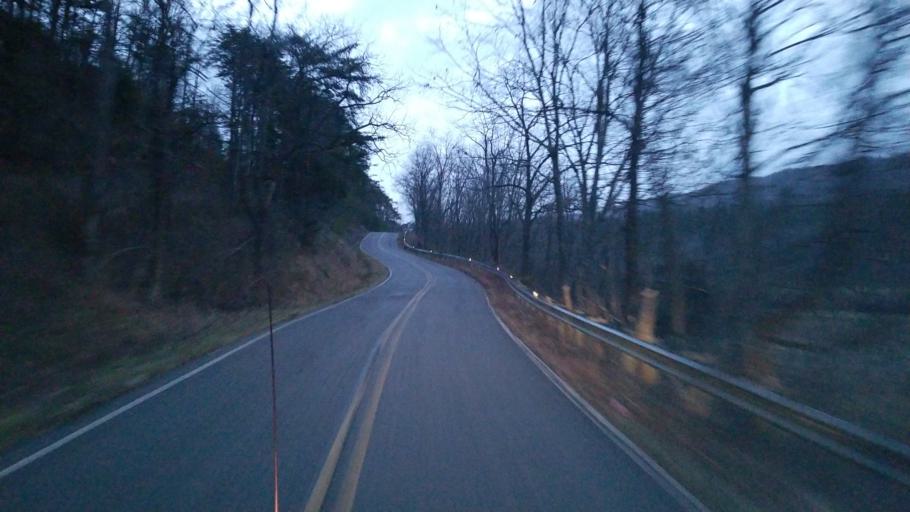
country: US
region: Virginia
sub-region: Pulaski County
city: Pulaski
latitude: 37.1423
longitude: -80.8417
